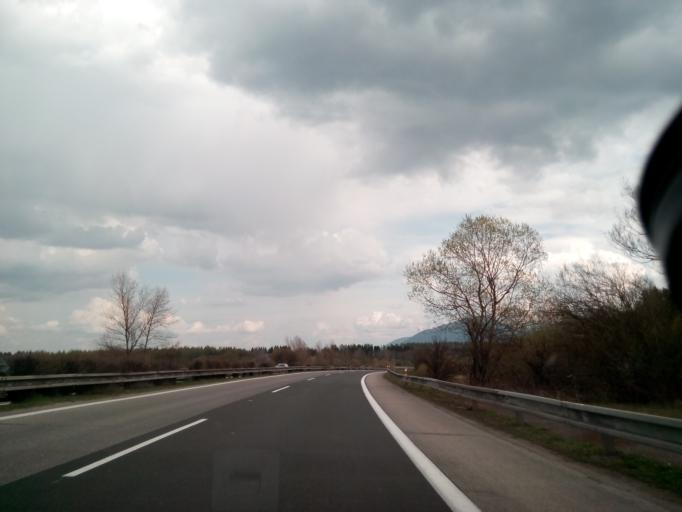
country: SK
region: Zilinsky
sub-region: Okres Liptovsky Mikulas
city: Liptovsky Mikulas
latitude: 49.0900
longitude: 19.4895
